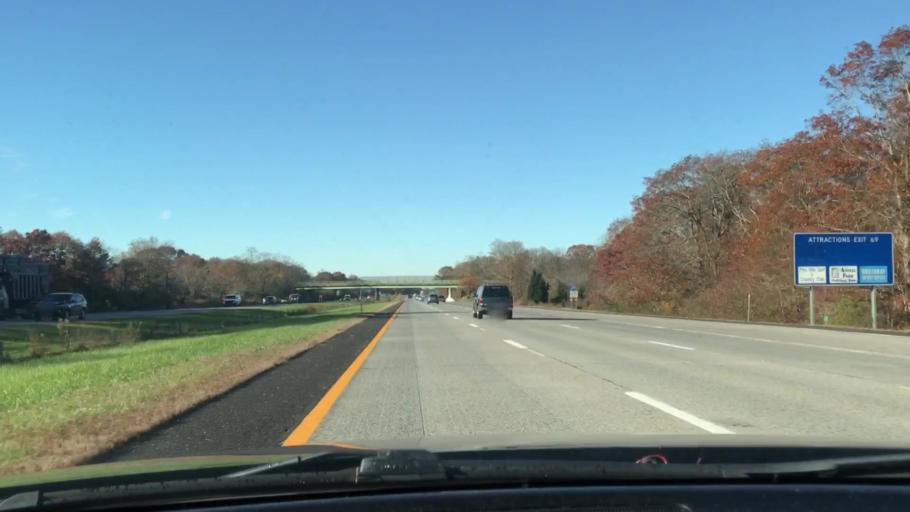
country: US
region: New York
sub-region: Suffolk County
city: Manorville
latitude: 40.8698
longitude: -72.8067
